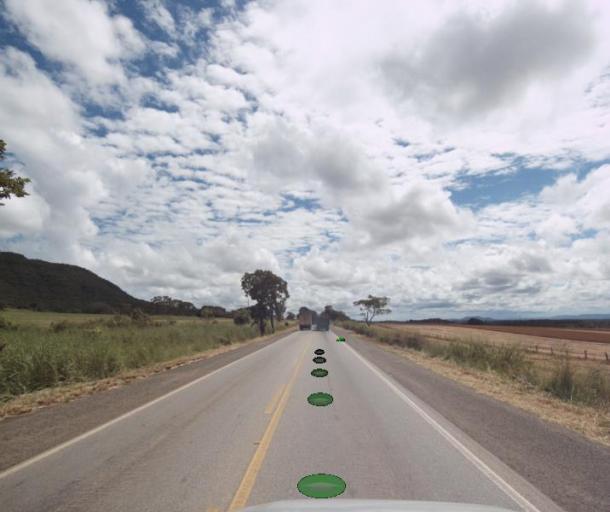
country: BR
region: Goias
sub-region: Uruacu
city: Uruacu
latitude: -14.3972
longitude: -49.1577
